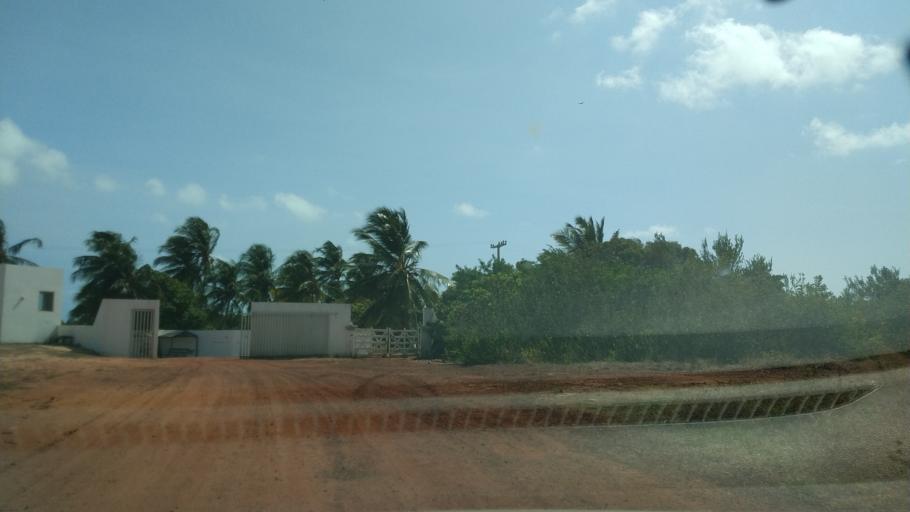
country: BR
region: Rio Grande do Norte
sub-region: Touros
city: Touros
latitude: -5.1603
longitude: -35.4955
